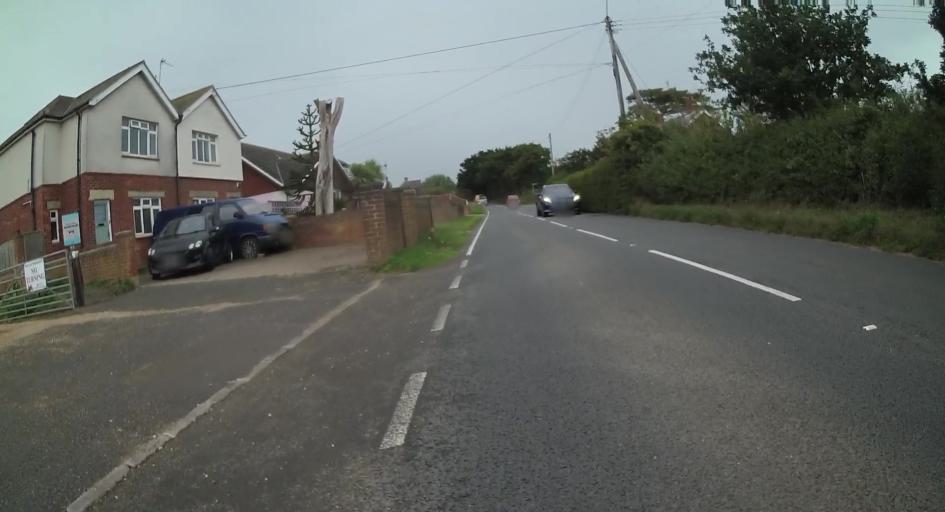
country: GB
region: England
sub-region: Isle of Wight
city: Newport
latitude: 50.6508
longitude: -1.2707
